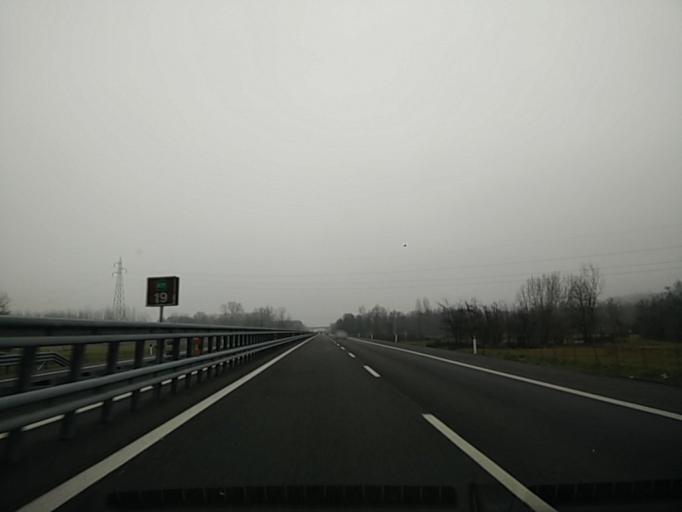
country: IT
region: Piedmont
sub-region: Provincia di Asti
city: Villafranca d'Asti
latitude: 44.9278
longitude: 8.0098
